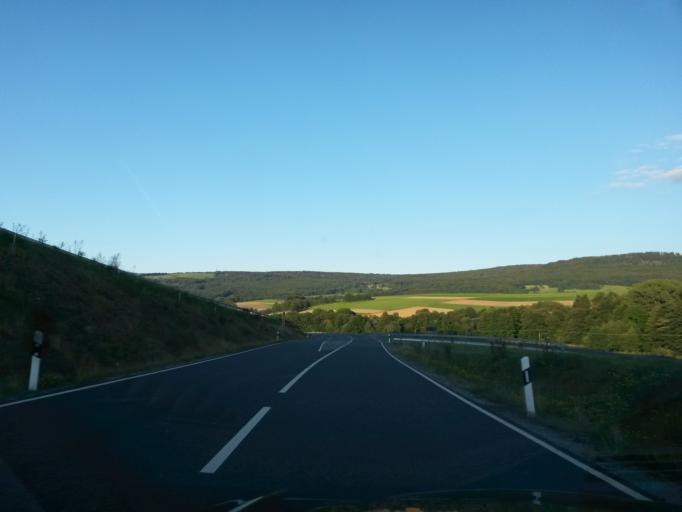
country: DE
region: Hesse
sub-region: Regierungsbezirk Kassel
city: Hilders
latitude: 50.5454
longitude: 9.9919
